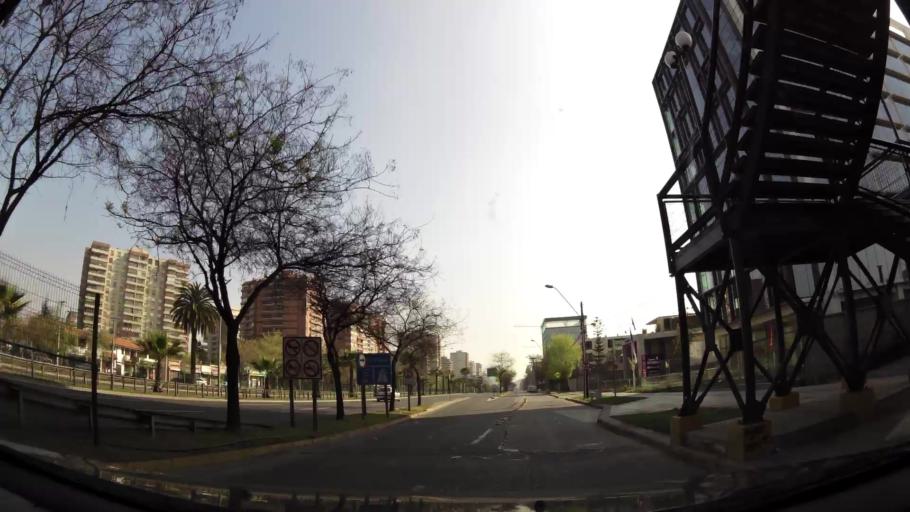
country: CL
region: Santiago Metropolitan
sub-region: Provincia de Santiago
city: Villa Presidente Frei, Nunoa, Santiago, Chile
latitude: -33.3916
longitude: -70.5535
